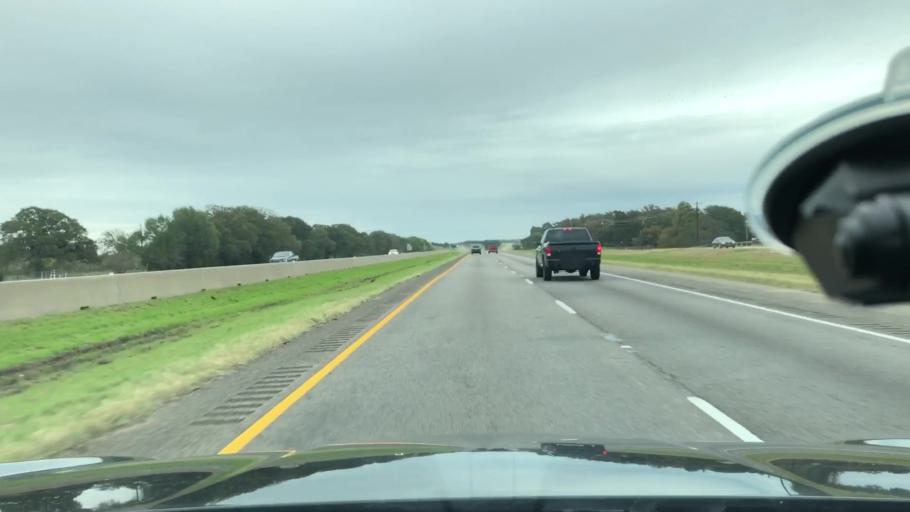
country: US
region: Texas
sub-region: Hopkins County
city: Sulphur Springs
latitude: 33.1467
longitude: -95.4760
